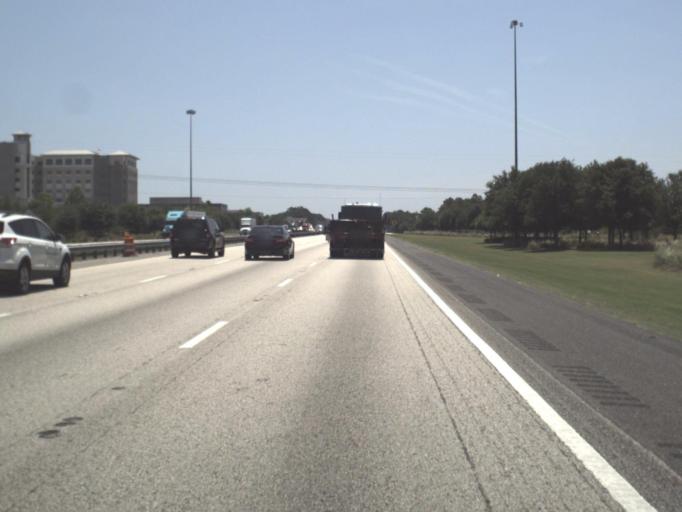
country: US
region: Florida
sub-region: Saint Johns County
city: Fruit Cove
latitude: 30.1399
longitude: -81.5394
